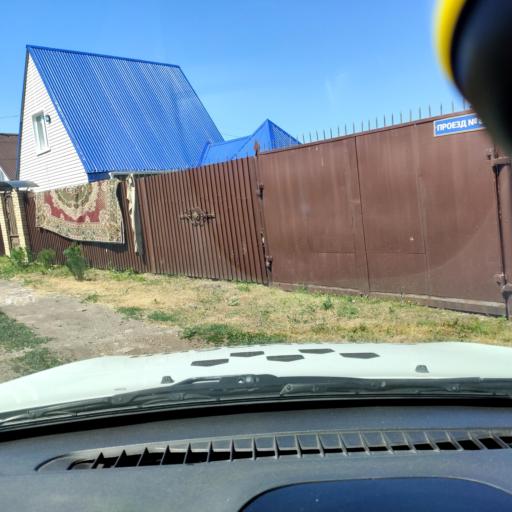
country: RU
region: Samara
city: Tol'yatti
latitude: 53.6109
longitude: 49.4499
